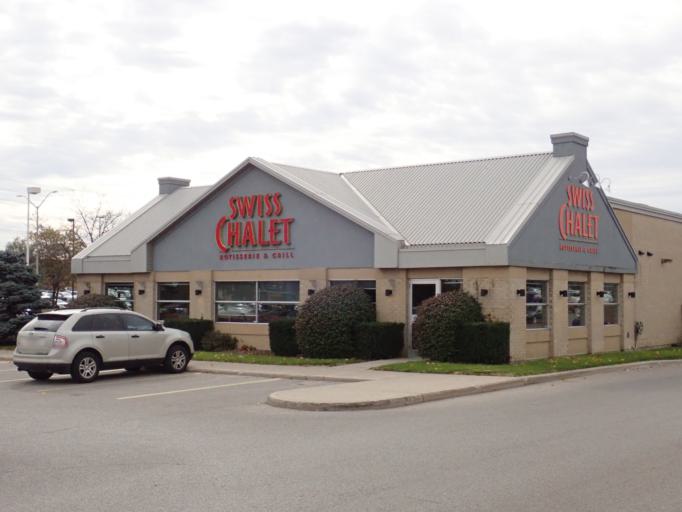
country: CA
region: Ontario
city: London
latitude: 43.0284
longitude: -81.2789
